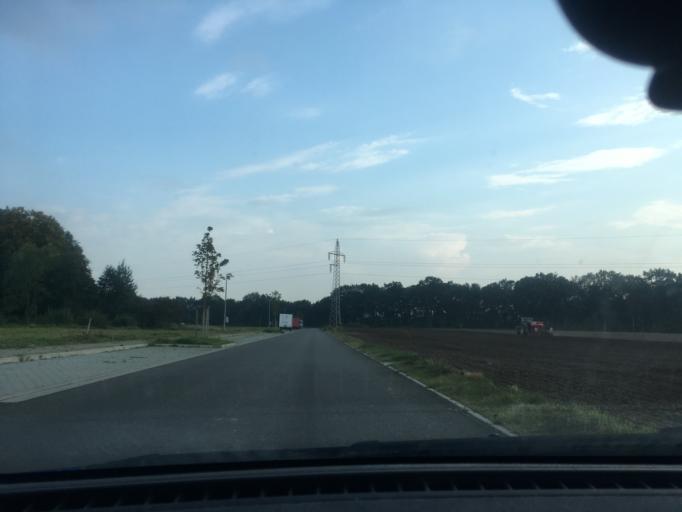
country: DE
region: Lower Saxony
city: Vastorf
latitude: 53.2067
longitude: 10.5290
